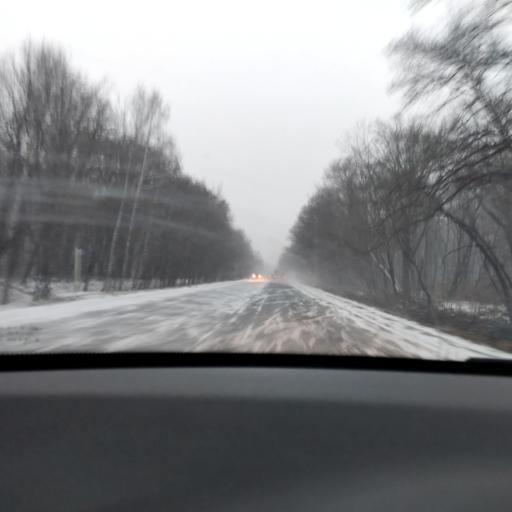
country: RU
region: Samara
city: Novokuybyshevsk
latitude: 52.9780
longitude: 49.8835
